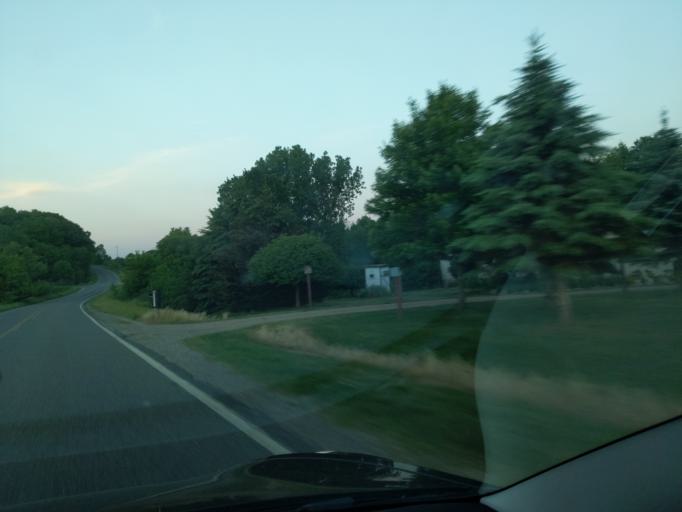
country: US
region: Michigan
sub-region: Barry County
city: Nashville
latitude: 42.5380
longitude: -85.0961
